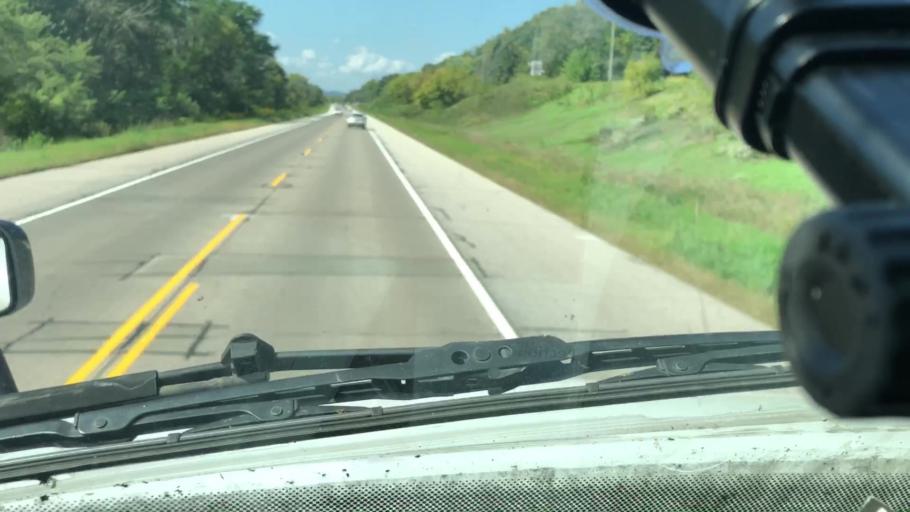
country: US
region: Minnesota
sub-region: Winona County
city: Winona
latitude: 44.0703
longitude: -91.6068
